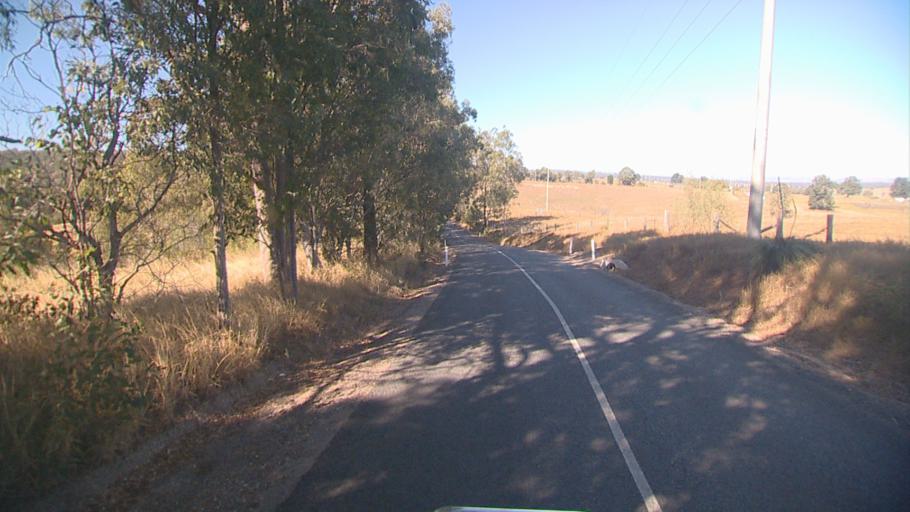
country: AU
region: Queensland
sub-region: Logan
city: Cedar Vale
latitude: -27.8971
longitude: 153.0149
